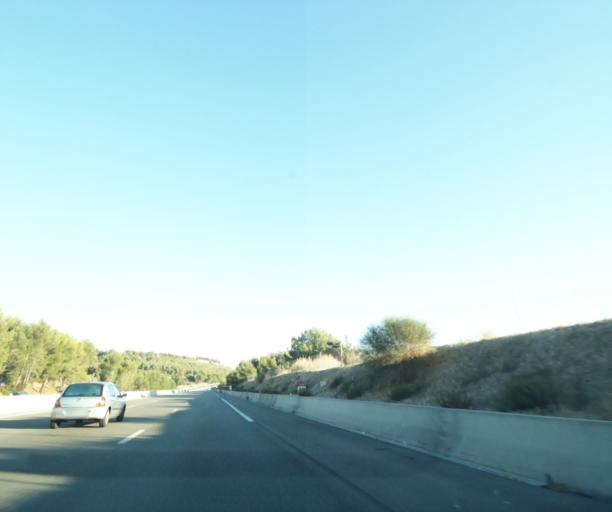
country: FR
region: Provence-Alpes-Cote d'Azur
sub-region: Departement des Bouches-du-Rhone
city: Ceyreste
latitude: 43.1969
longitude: 5.6423
